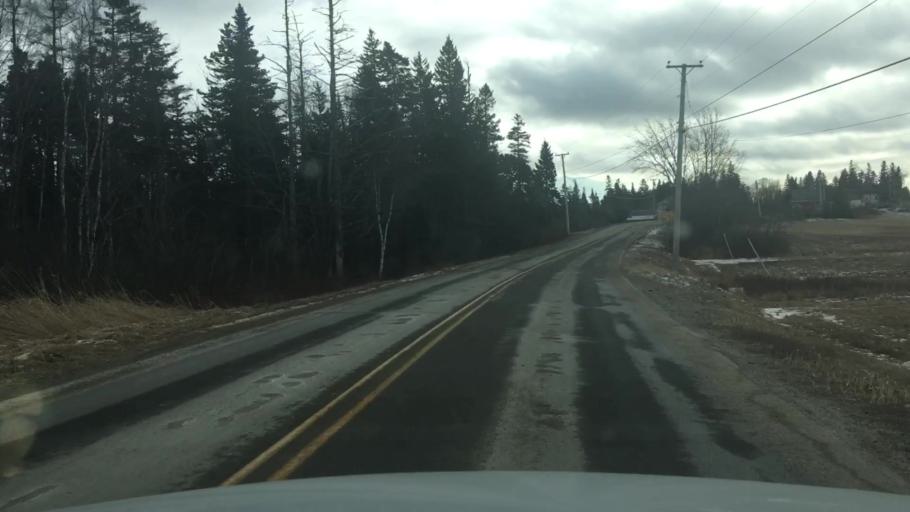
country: US
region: Maine
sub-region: Washington County
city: Machias
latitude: 44.6164
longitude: -67.4793
